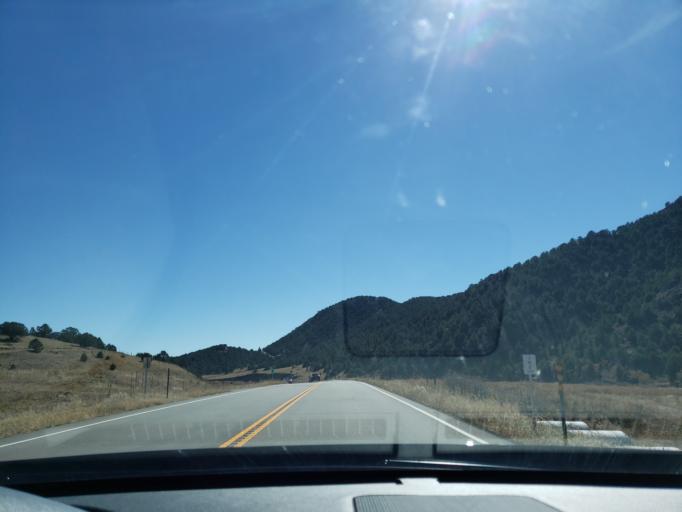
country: US
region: Colorado
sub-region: Fremont County
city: Canon City
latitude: 38.6239
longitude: -105.4565
